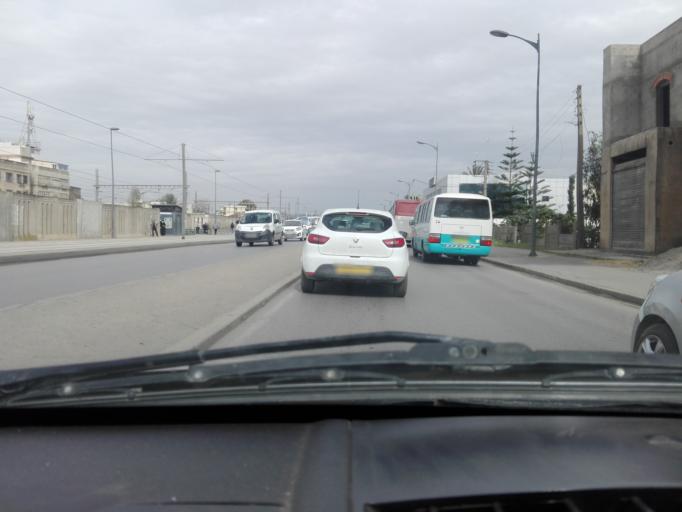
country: DZ
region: Alger
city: Bab Ezzouar
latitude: 36.7321
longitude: 3.1256
